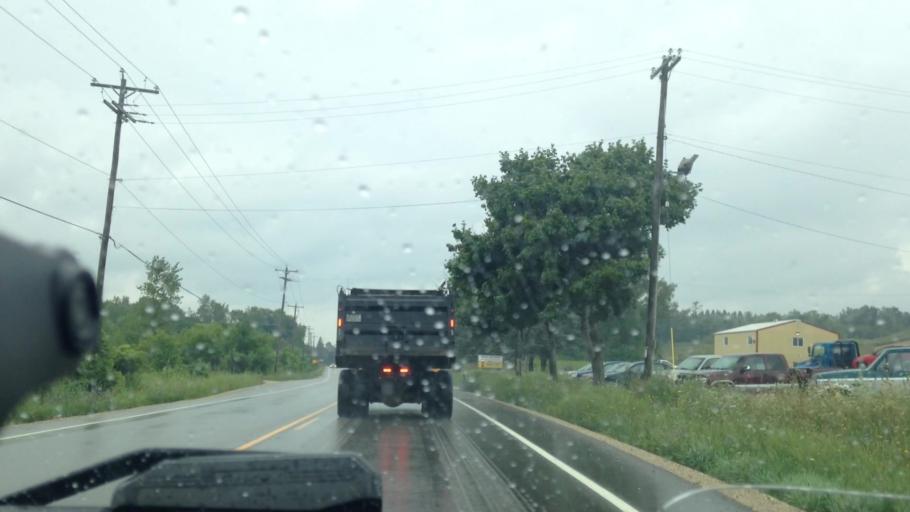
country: US
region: Wisconsin
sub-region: Washington County
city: Richfield
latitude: 43.2325
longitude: -88.1847
